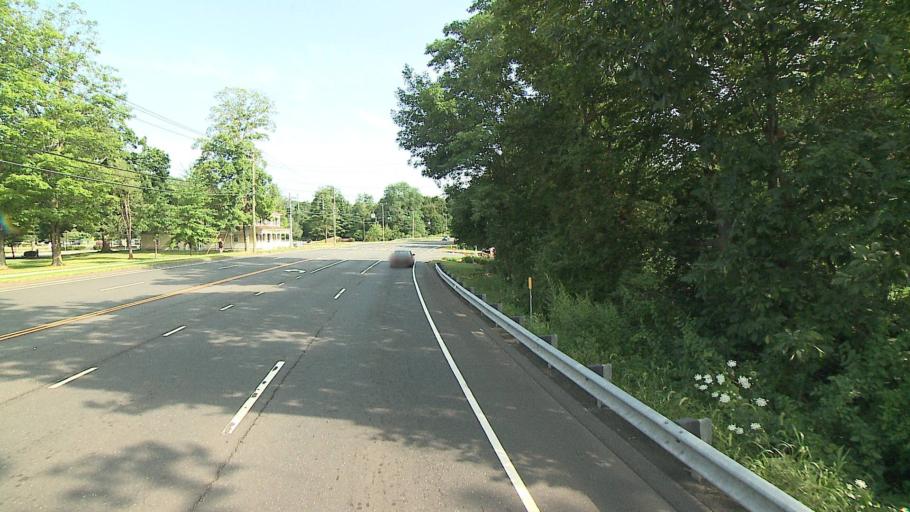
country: US
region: Connecticut
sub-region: Fairfield County
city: Wilton
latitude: 41.2114
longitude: -73.4320
